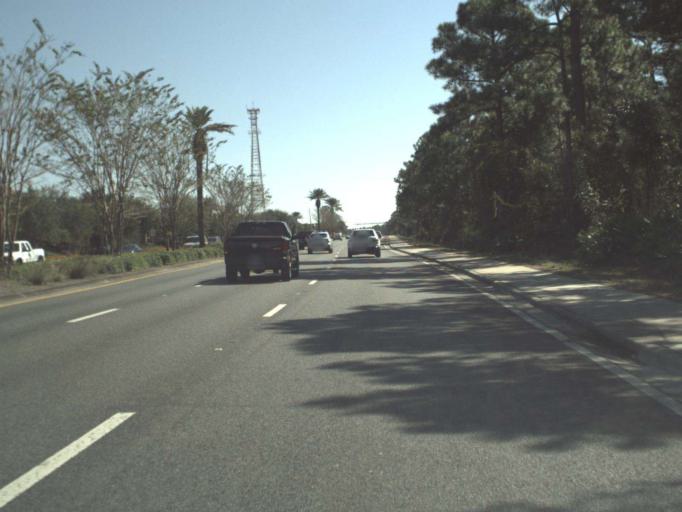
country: US
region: Florida
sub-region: Walton County
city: Miramar Beach
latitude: 30.3781
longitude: -86.3144
